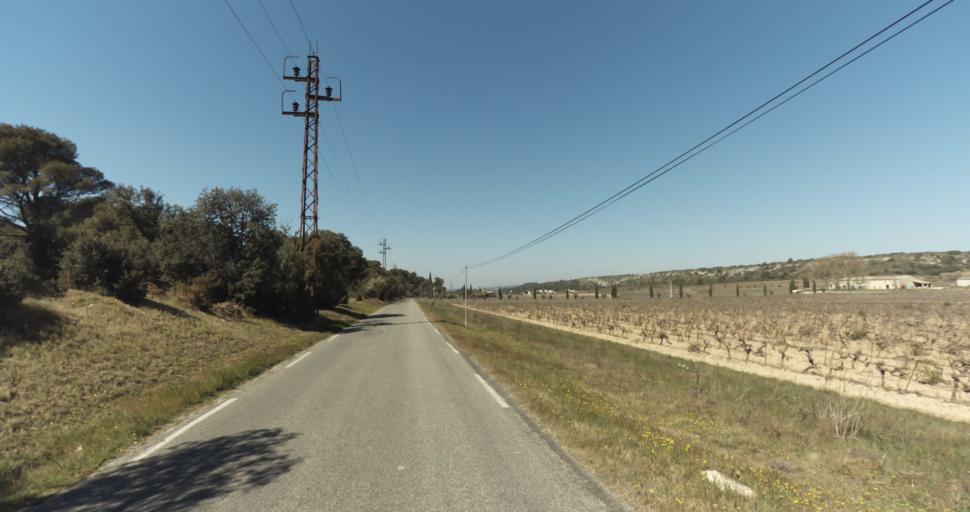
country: FR
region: Provence-Alpes-Cote d'Azur
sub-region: Departement des Bouches-du-Rhone
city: La Fare-les-Oliviers
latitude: 43.6014
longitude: 5.1953
